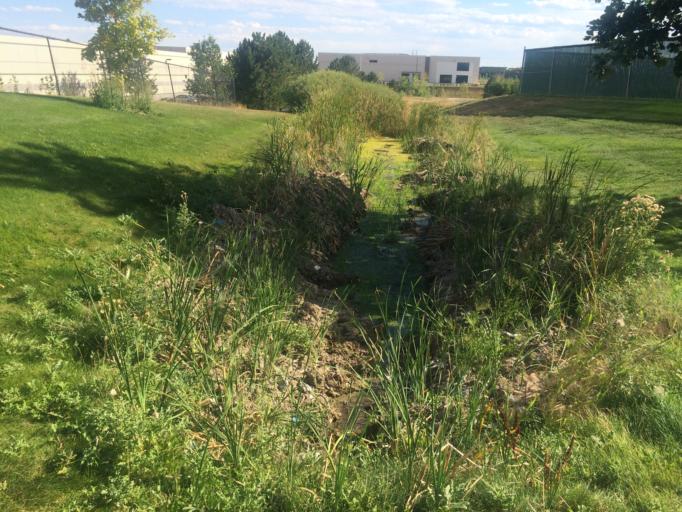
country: US
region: Colorado
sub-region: Broomfield County
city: Broomfield
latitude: 39.9059
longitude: -105.0744
